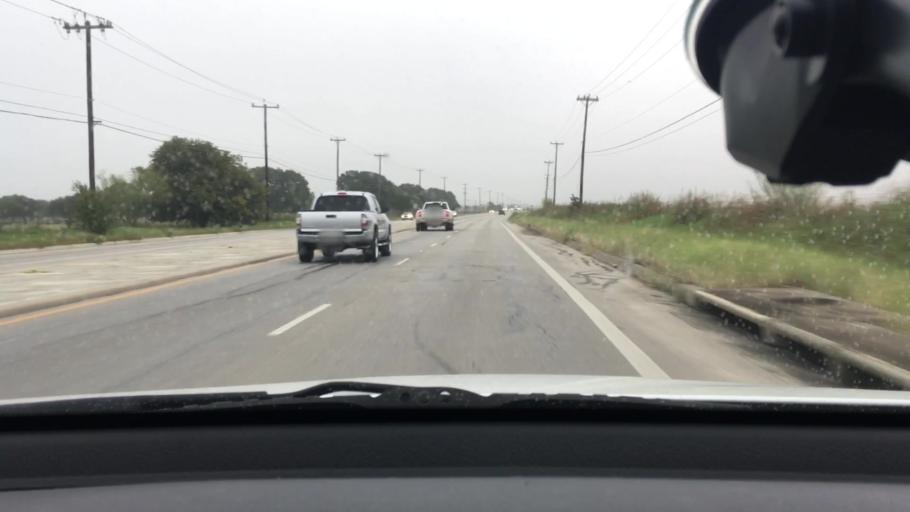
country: US
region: Texas
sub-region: Bexar County
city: Live Oak
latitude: 29.5980
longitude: -98.3398
